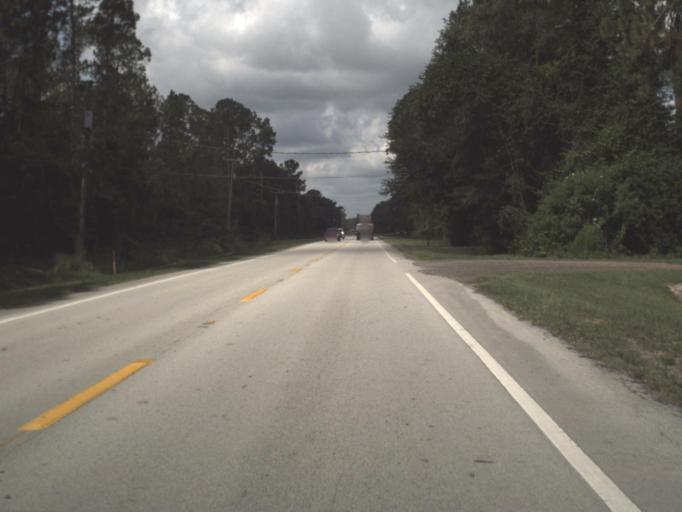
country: US
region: Florida
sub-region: Baker County
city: Macclenny
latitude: 30.2459
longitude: -82.1290
